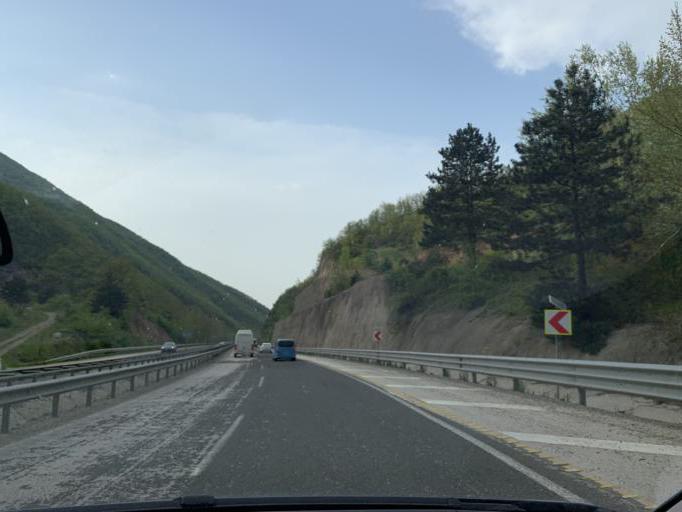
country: TR
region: Bursa
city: Kursunlu
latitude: 39.9976
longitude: 29.6538
